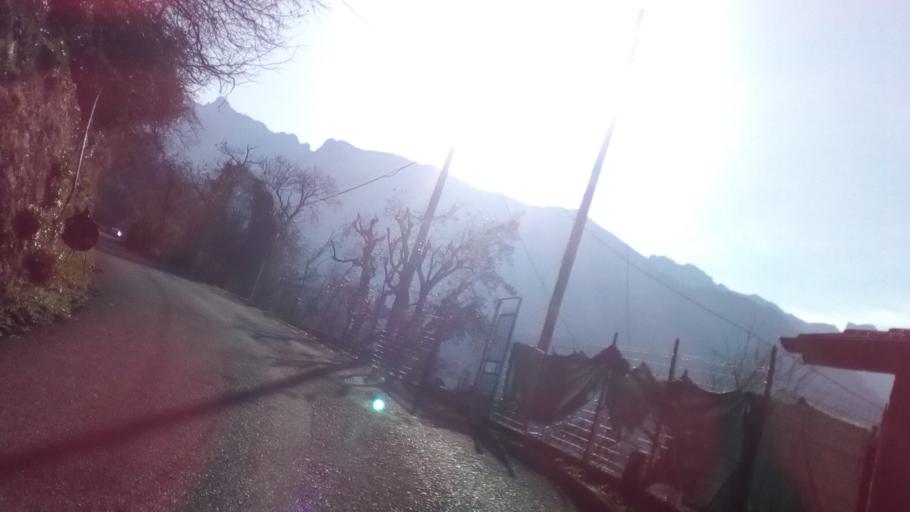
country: IT
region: Tuscany
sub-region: Provincia di Massa-Carrara
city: Montignoso
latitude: 44.0574
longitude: 10.1857
